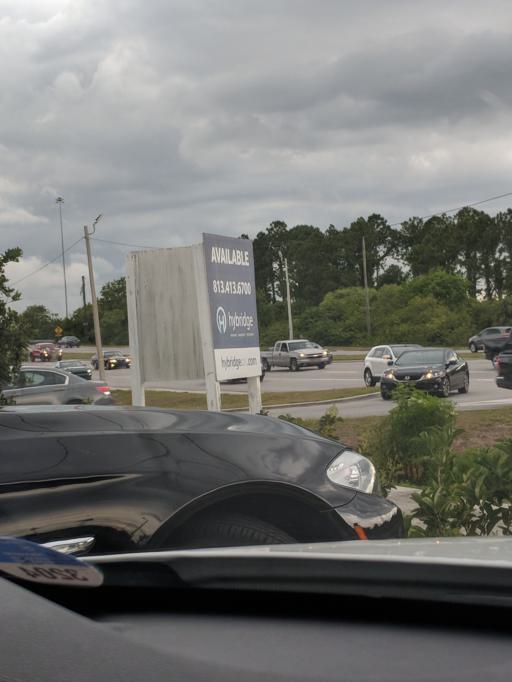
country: US
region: Florida
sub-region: Hillsborough County
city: Progress Village
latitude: 27.9224
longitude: -82.3291
